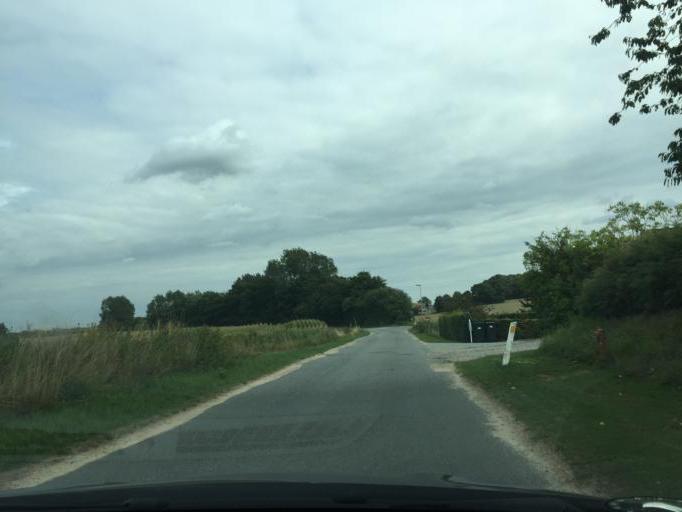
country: DK
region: South Denmark
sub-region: Assens Kommune
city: Vissenbjerg
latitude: 55.3491
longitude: 10.0990
